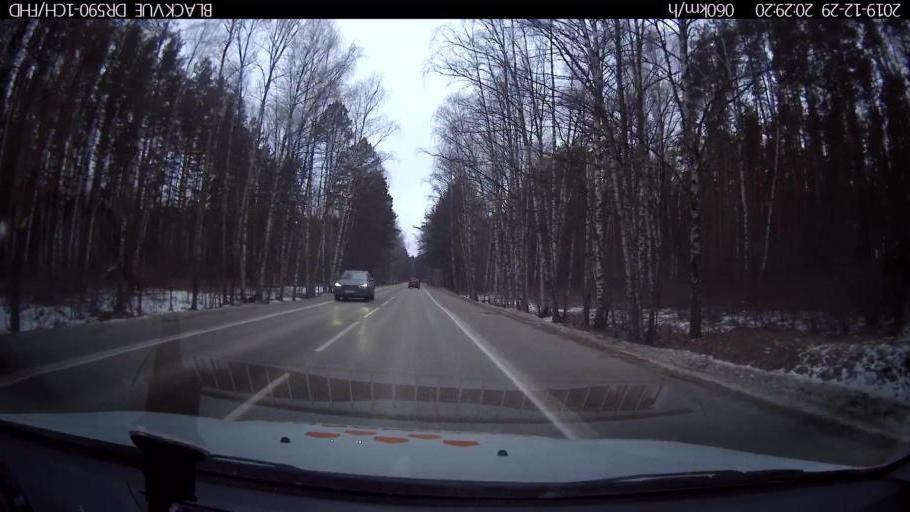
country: RU
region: Nizjnij Novgorod
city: Afonino
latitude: 56.1814
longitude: 44.1043
